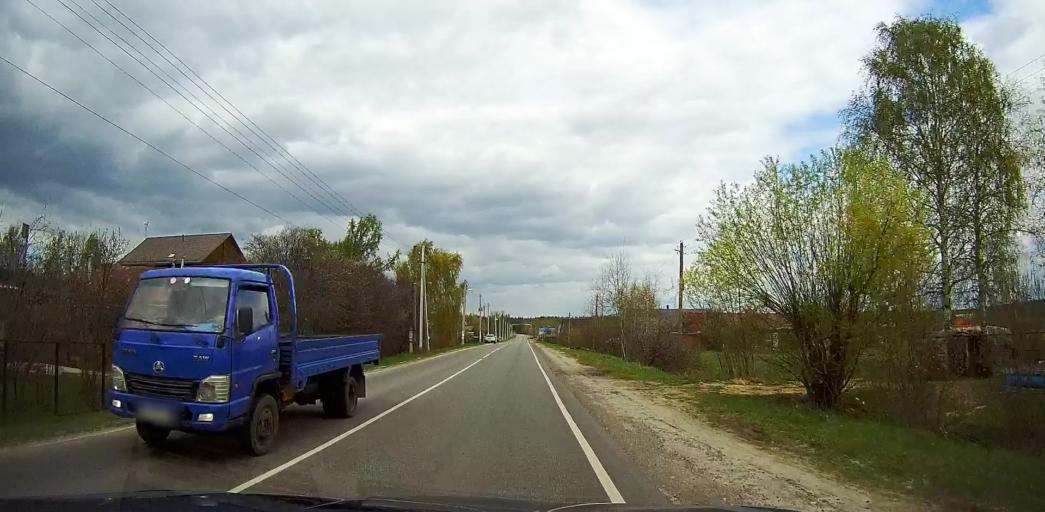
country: RU
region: Moskovskaya
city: Ashitkovo
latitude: 55.4627
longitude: 38.6049
